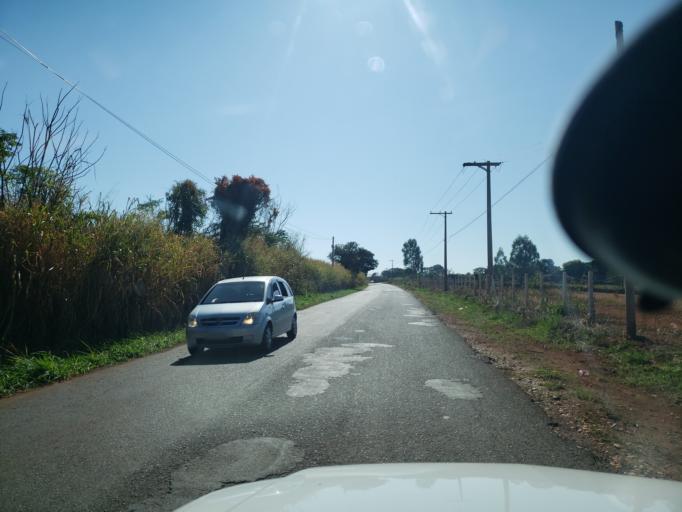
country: BR
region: Sao Paulo
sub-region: Moji-Guacu
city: Mogi-Gaucu
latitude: -22.3471
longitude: -46.8929
